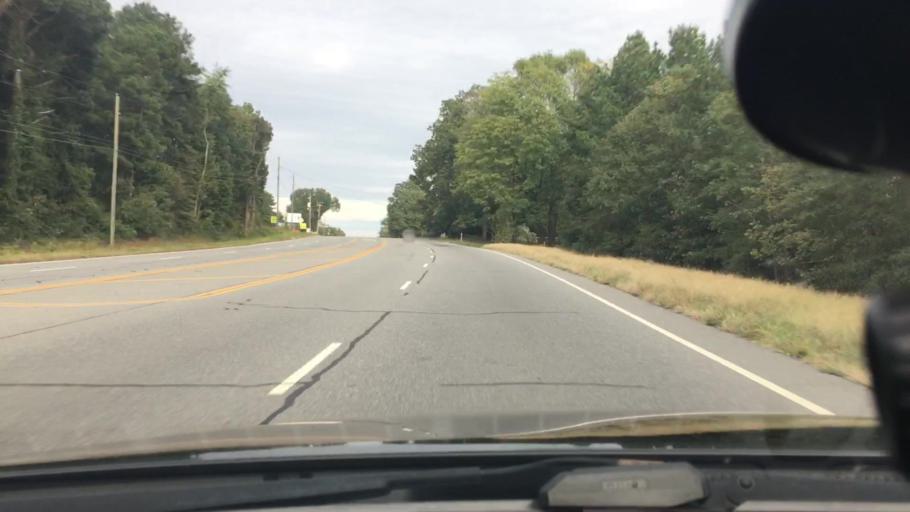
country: US
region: North Carolina
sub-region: Montgomery County
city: Biscoe
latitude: 35.3550
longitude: -79.8127
